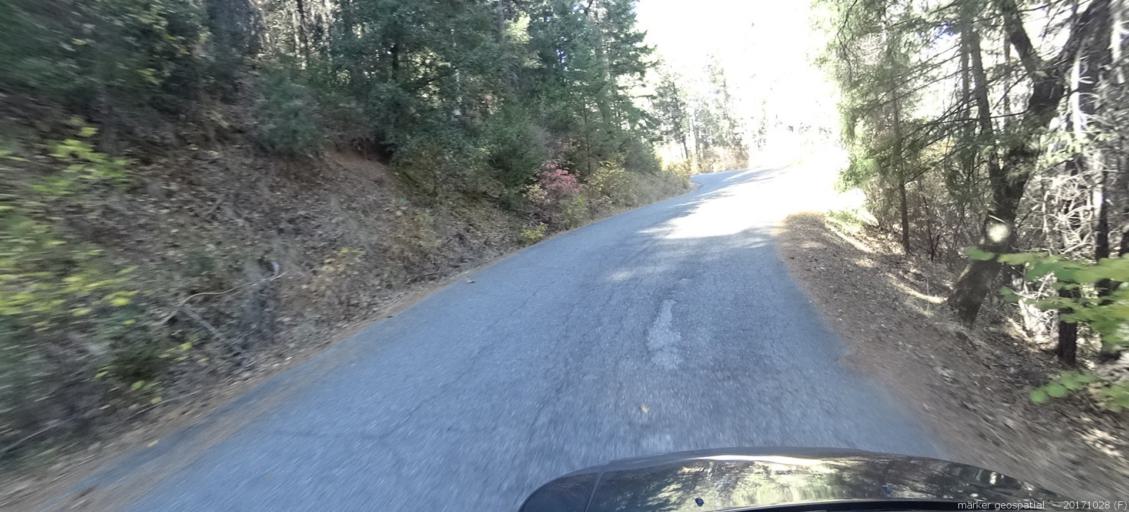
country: US
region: California
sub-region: Trinity County
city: Lewiston
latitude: 40.8104
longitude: -122.6258
